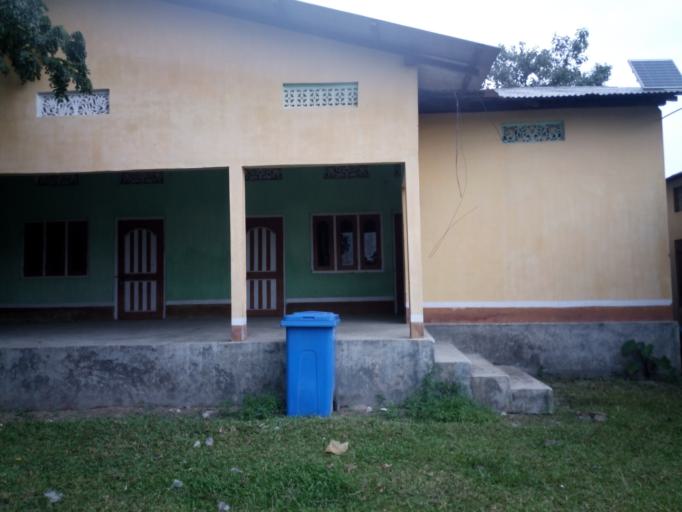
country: IN
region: Assam
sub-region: Darrang
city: Kharupatia
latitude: 26.6416
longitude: 92.2490
